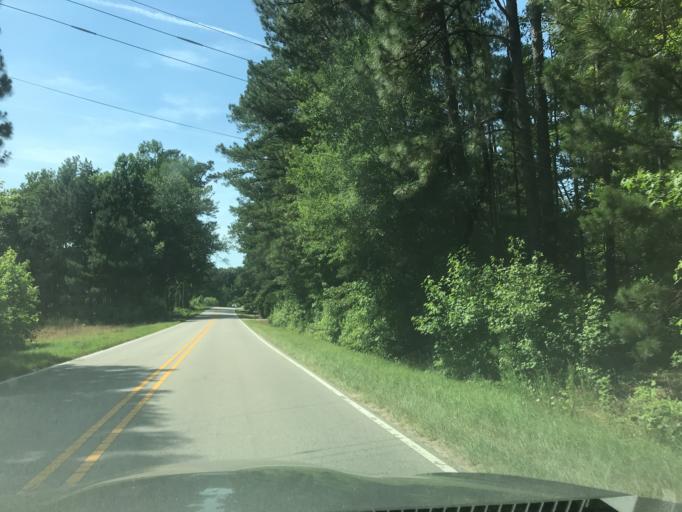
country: US
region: North Carolina
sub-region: Wake County
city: Wendell
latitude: 35.7688
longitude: -78.3558
